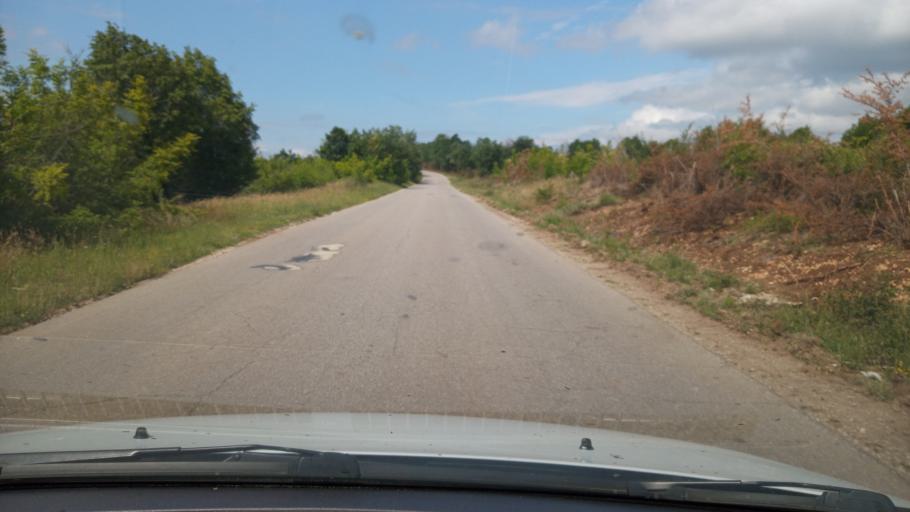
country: BG
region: Lovech
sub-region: Obshtina Lukovit
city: Lukovit
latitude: 43.2026
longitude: 24.1295
